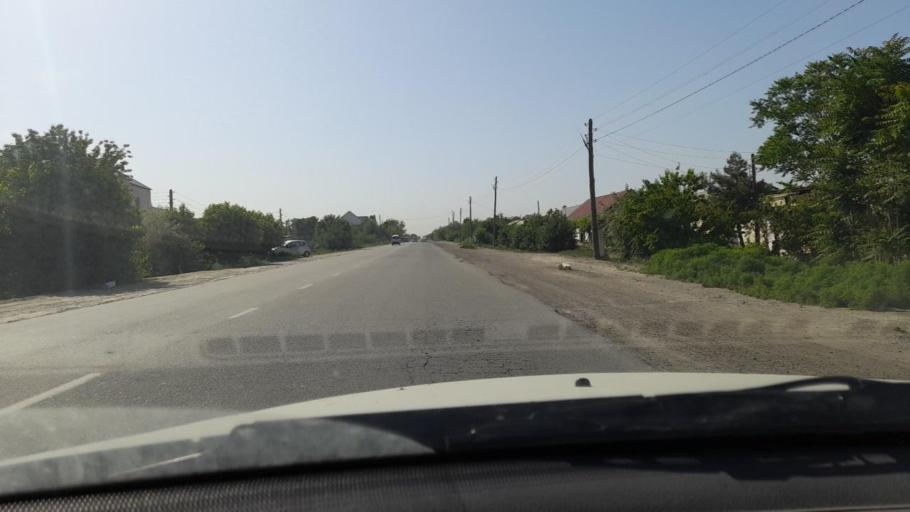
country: UZ
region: Bukhara
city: Romiton
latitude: 39.9040
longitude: 64.4030
